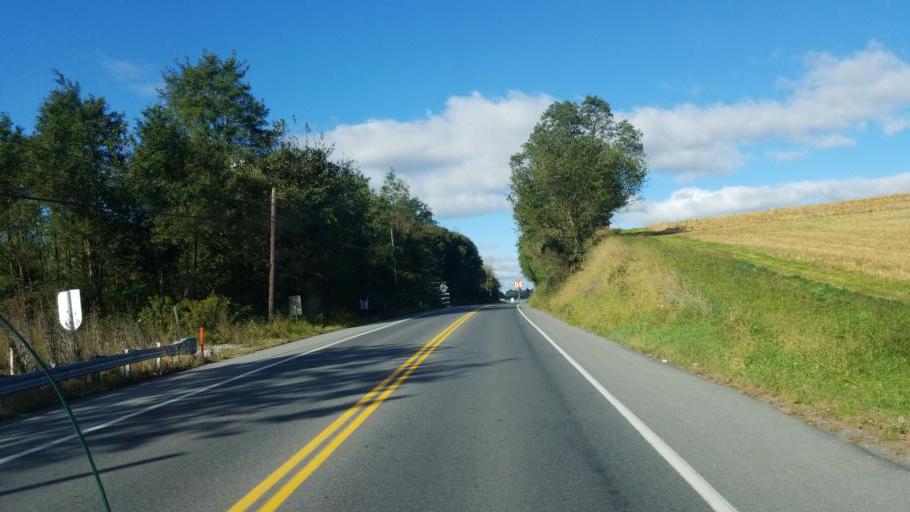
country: US
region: Pennsylvania
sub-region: Franklin County
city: Waynesboro
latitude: 39.7630
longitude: -77.6010
